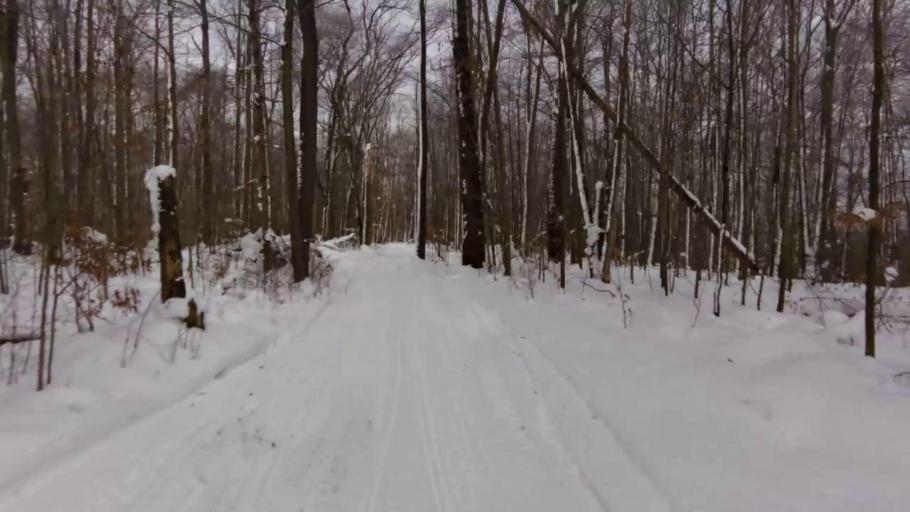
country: US
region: New York
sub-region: Cattaraugus County
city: Salamanca
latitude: 42.0371
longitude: -78.7539
